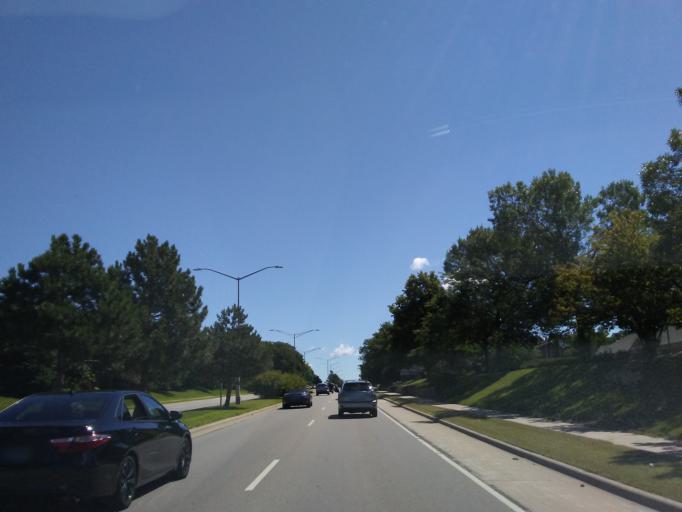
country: US
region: Wisconsin
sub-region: Dane County
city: Fitchburg
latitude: 43.0153
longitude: -89.4543
